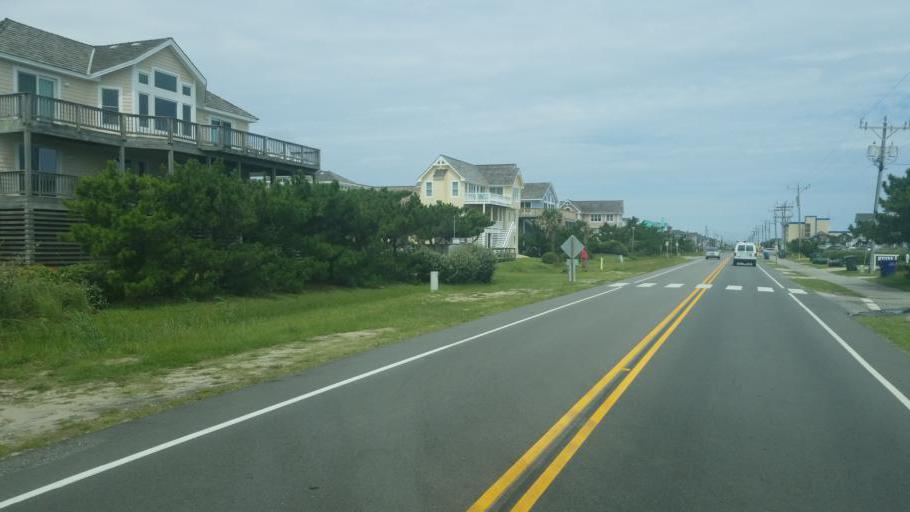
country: US
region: North Carolina
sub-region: Dare County
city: Nags Head
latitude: 35.9411
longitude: -75.6150
